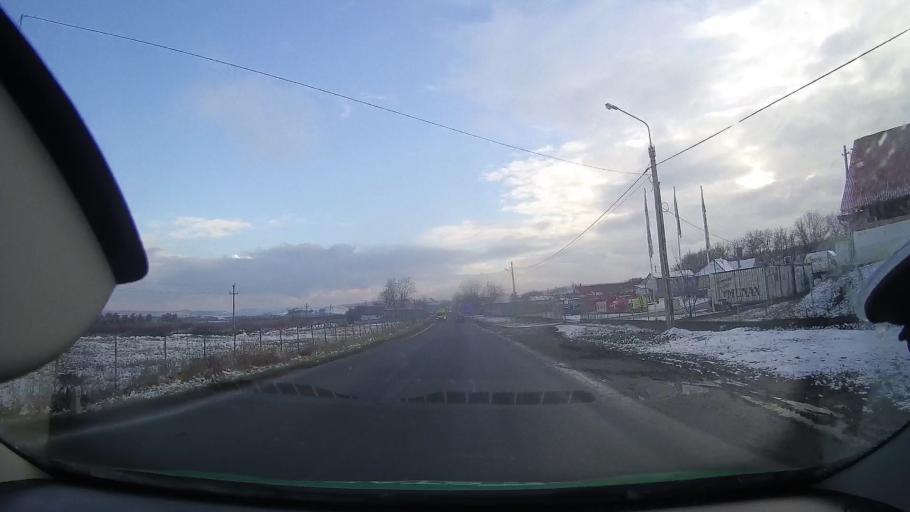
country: RO
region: Mures
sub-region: Comuna Iernut
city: Iernut
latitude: 46.4337
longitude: 24.2542
